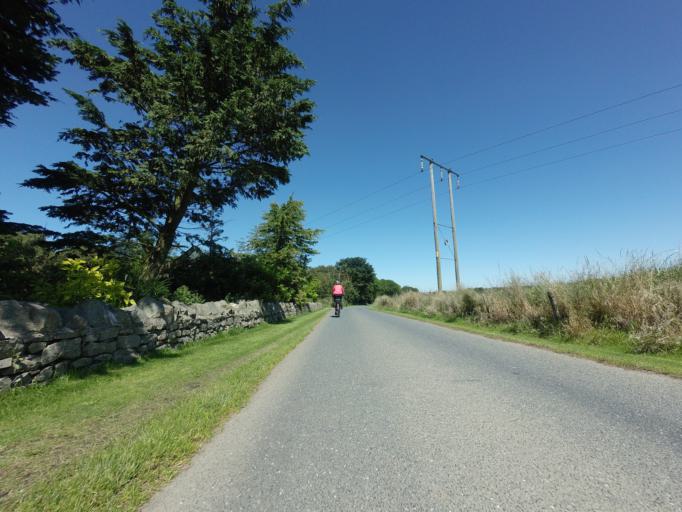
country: GB
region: Scotland
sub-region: Aberdeenshire
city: Macduff
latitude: 57.6581
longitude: -2.4981
